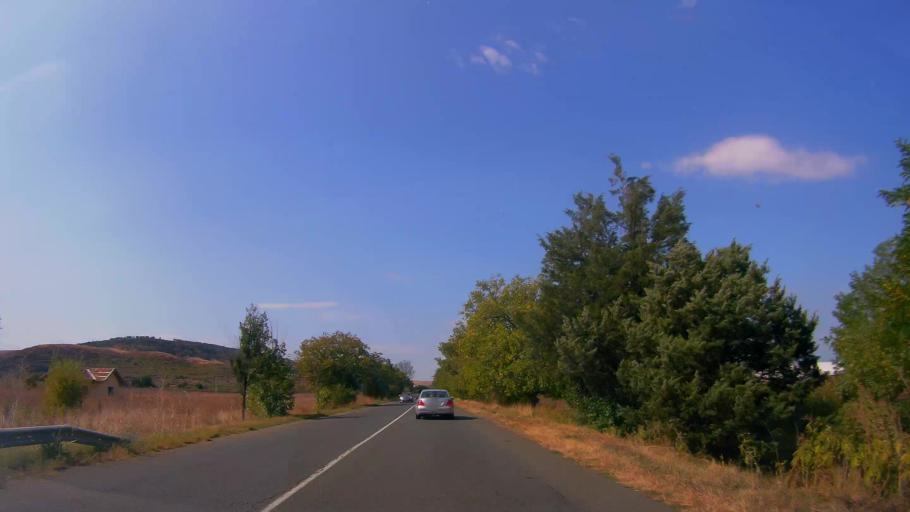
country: BG
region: Burgas
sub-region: Obshtina Karnobat
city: Karnobat
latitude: 42.6566
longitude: 27.0147
